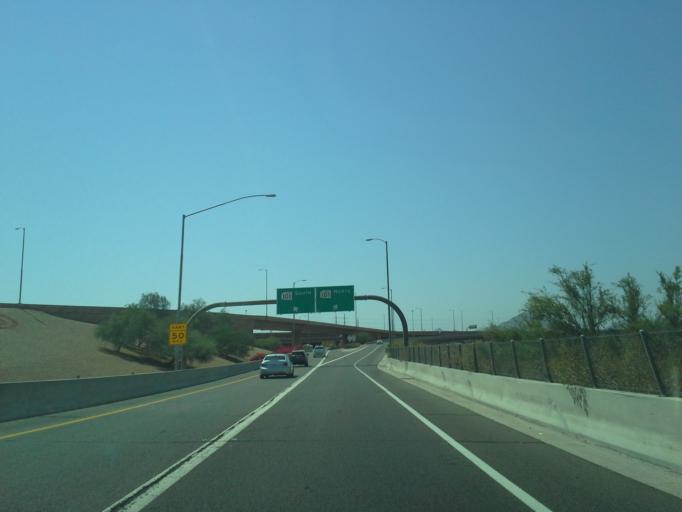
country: US
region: Arizona
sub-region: Maricopa County
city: Tempe
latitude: 33.4344
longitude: -111.8872
